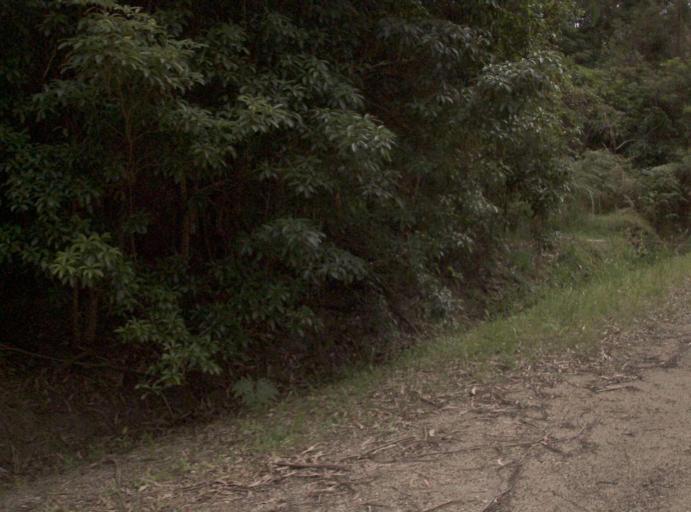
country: AU
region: New South Wales
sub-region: Bombala
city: Bombala
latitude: -37.4615
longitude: 149.1872
